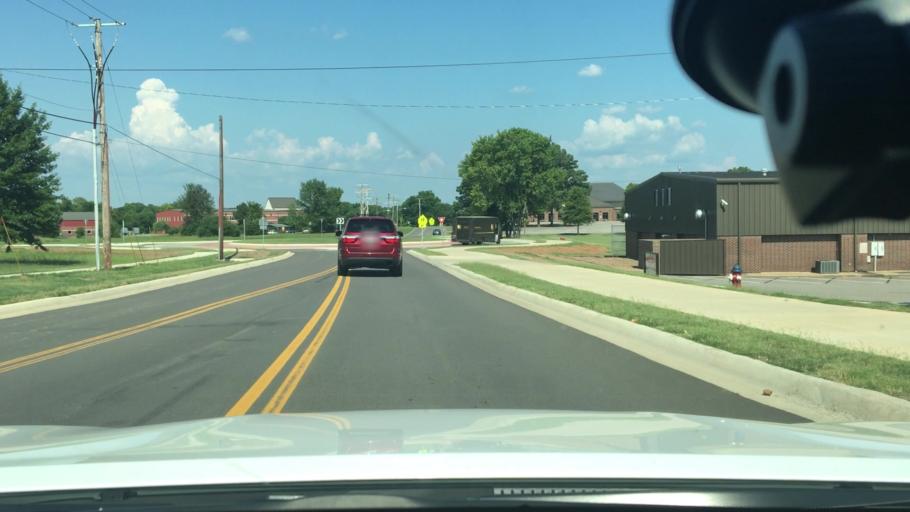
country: US
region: Arkansas
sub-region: Johnson County
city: Clarksville
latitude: 35.4617
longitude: -93.4864
